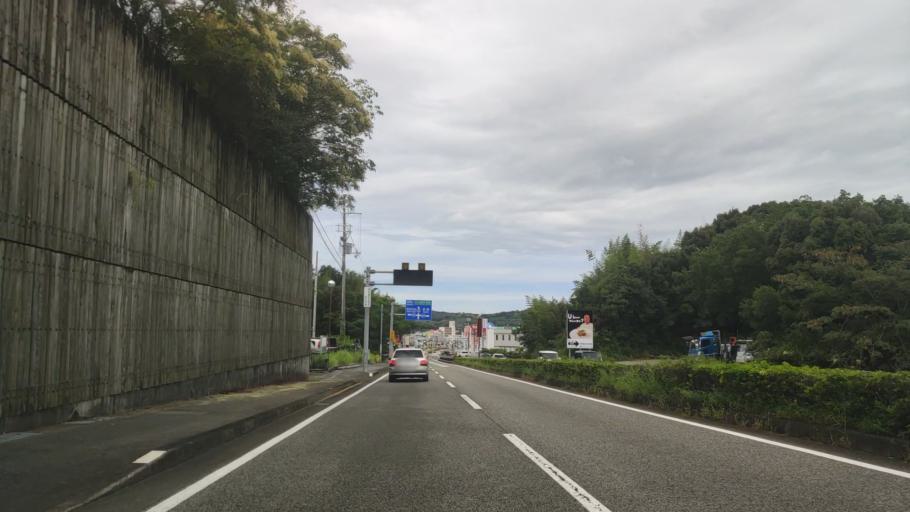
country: JP
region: Wakayama
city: Tanabe
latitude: 33.7365
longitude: 135.3983
